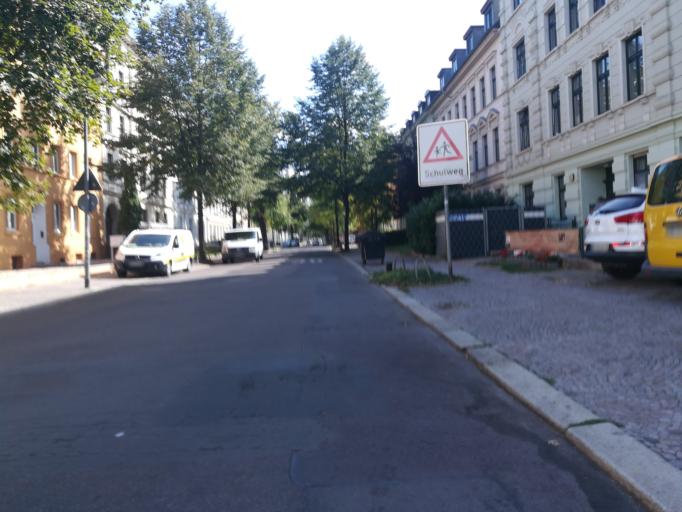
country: DE
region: Saxony-Anhalt
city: Magdeburg
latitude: 52.1322
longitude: 11.6083
